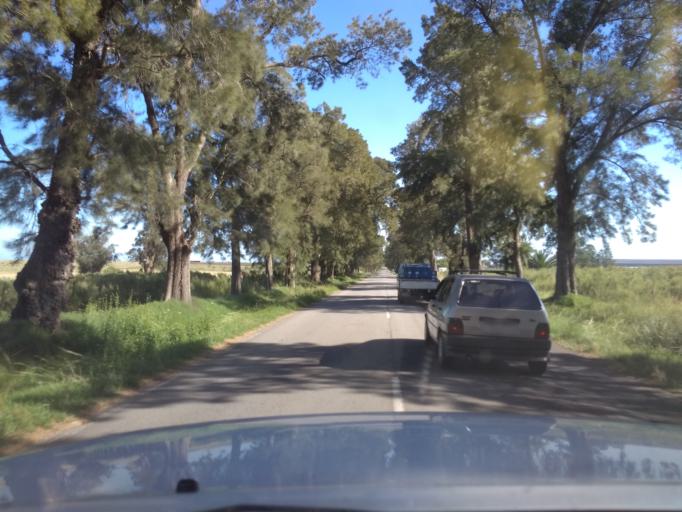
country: UY
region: Canelones
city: San Bautista
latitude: -34.3935
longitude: -55.9596
